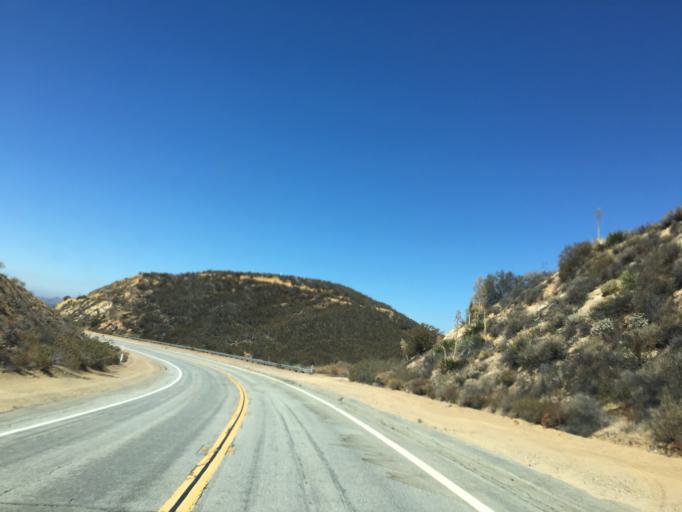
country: US
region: California
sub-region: Los Angeles County
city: Castaic
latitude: 34.5441
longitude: -118.5584
